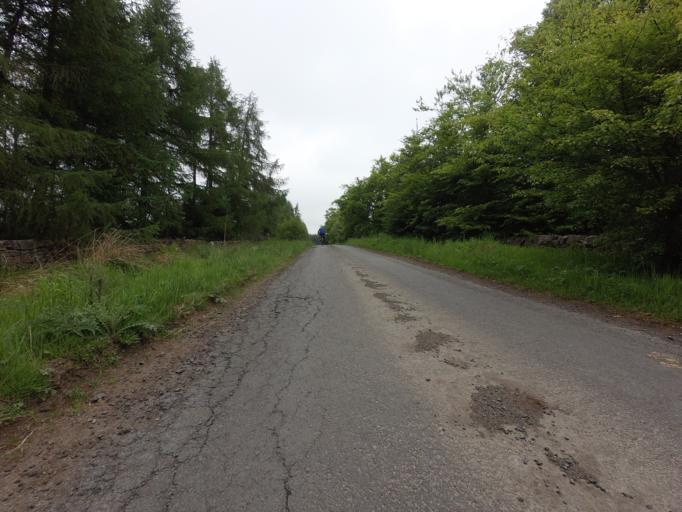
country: GB
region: Scotland
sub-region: Fife
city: Townhill
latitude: 56.1375
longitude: -3.4445
